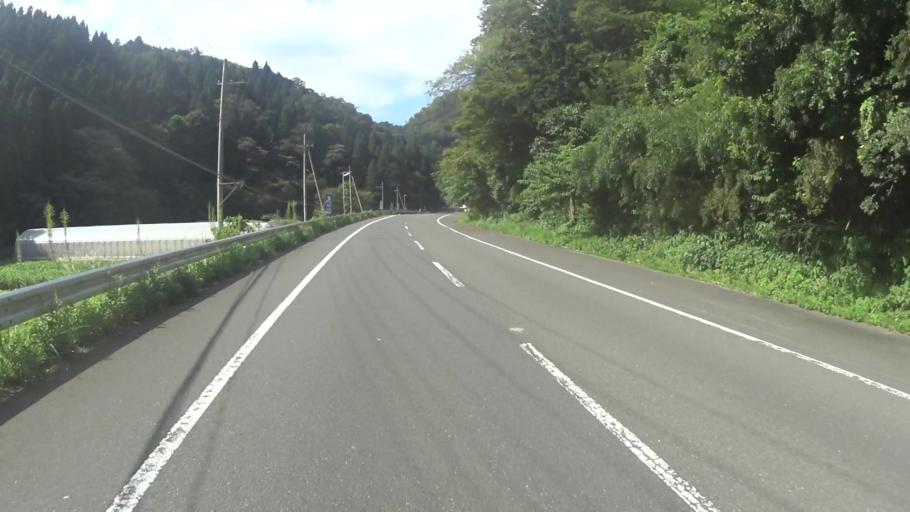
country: JP
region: Kyoto
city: Miyazu
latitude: 35.7339
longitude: 135.2565
